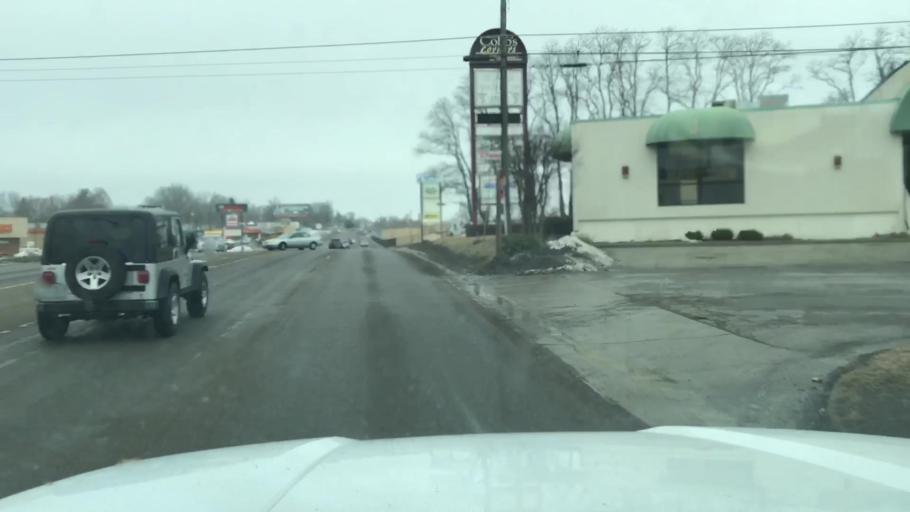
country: US
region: Missouri
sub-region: Buchanan County
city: Saint Joseph
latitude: 39.7882
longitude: -94.8062
